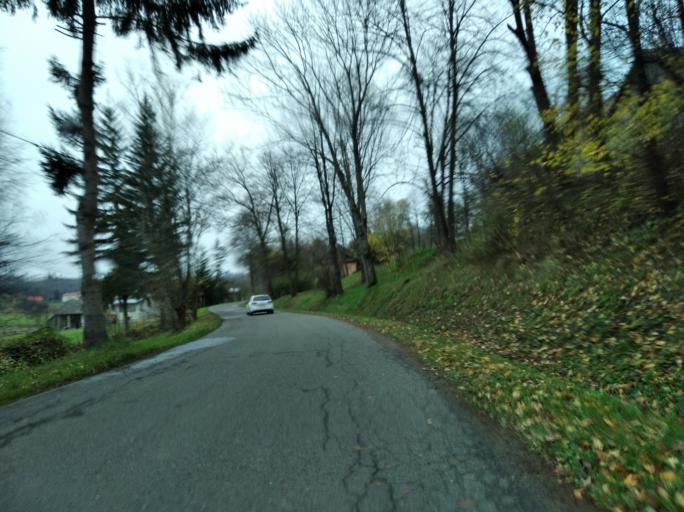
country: PL
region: Subcarpathian Voivodeship
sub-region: Powiat strzyzowski
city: Frysztak
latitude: 49.8347
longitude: 21.6262
